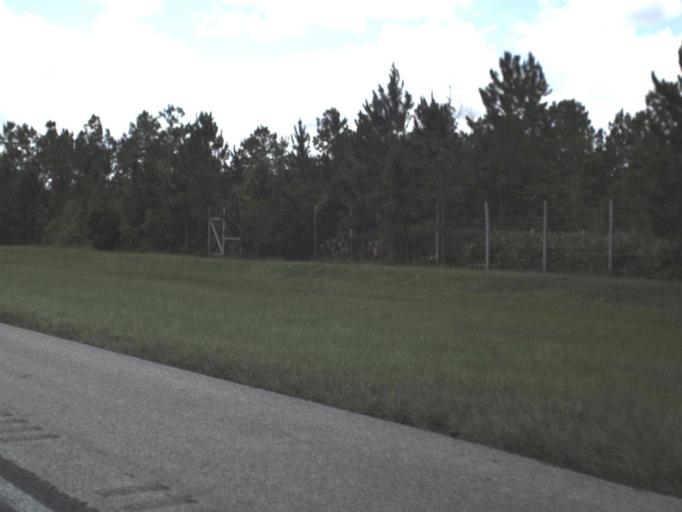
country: US
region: Florida
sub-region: Saint Johns County
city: Saint Augustine Shores
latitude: 29.7540
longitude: -81.3491
